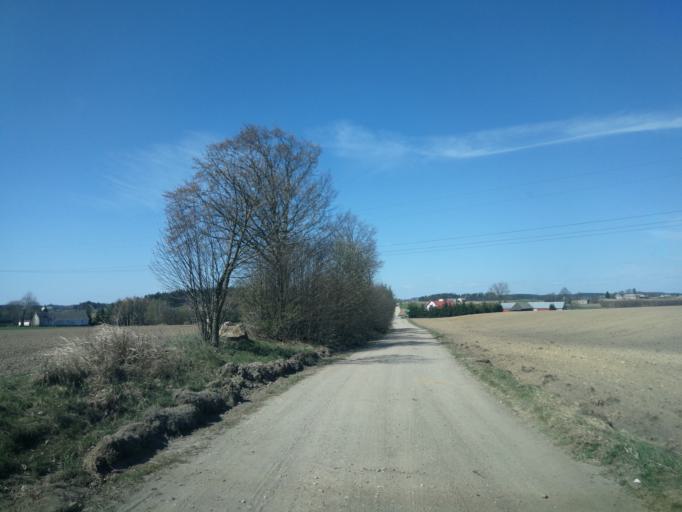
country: PL
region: Warmian-Masurian Voivodeship
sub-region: Powiat dzialdowski
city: Rybno
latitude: 53.4386
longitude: 19.9478
